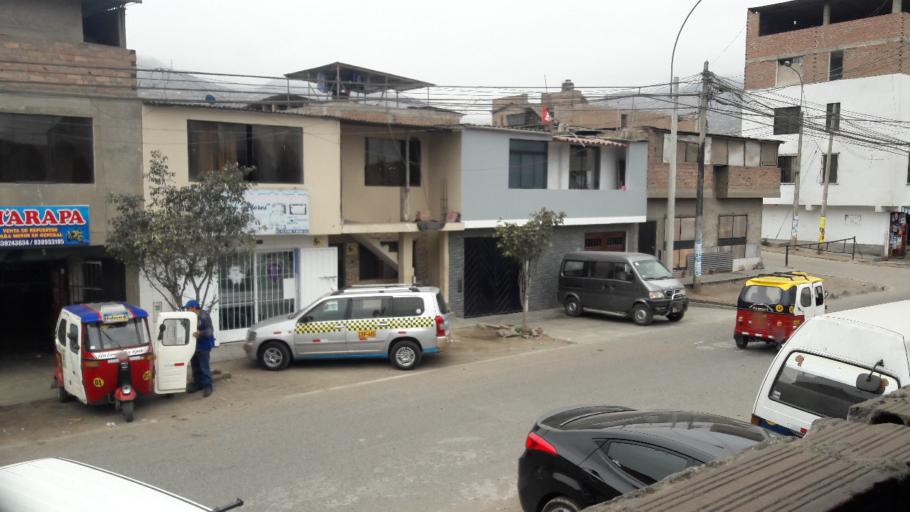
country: PE
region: Lima
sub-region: Lima
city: Surco
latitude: -12.1442
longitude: -76.9537
